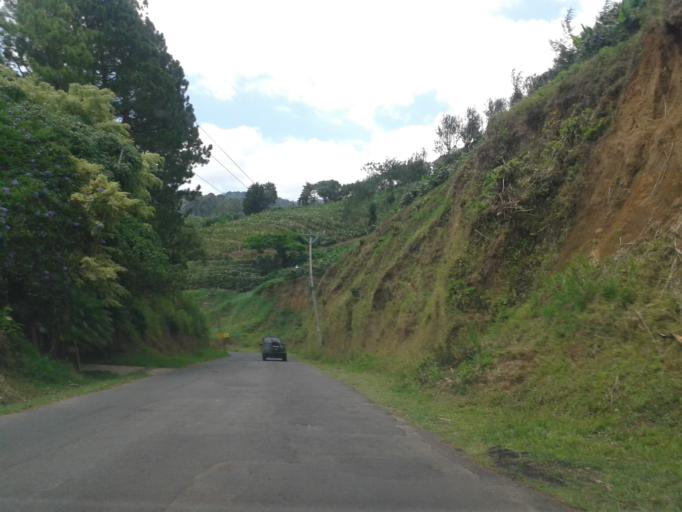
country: CR
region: Alajuela
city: Sabanilla
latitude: 10.0980
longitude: -84.1918
